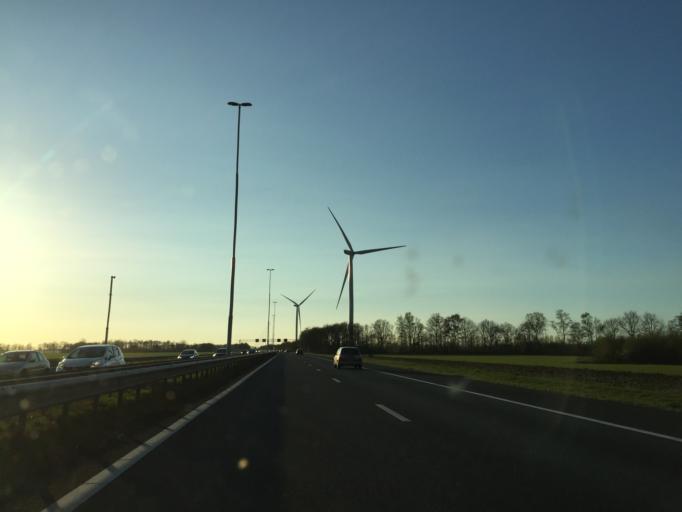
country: NL
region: North Brabant
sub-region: Gemeente Oirschot
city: Middelbeers
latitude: 51.5196
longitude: 5.2366
